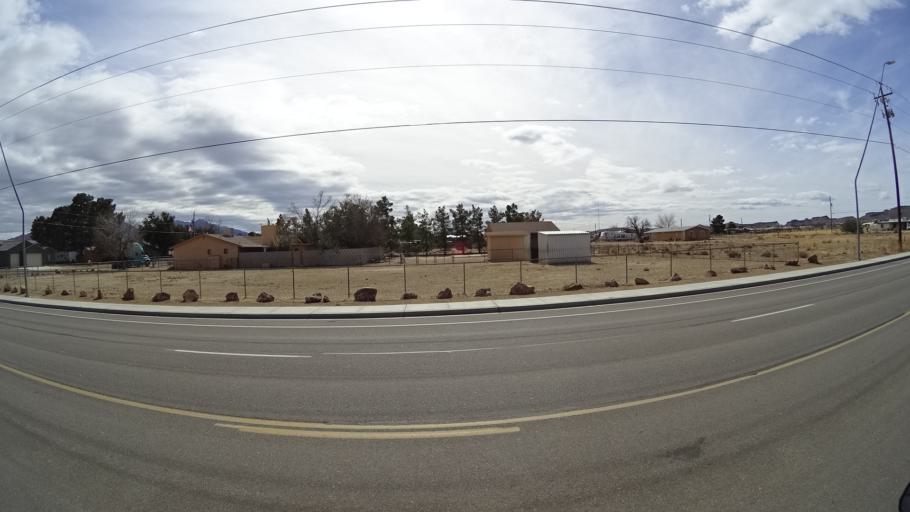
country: US
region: Arizona
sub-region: Mohave County
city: New Kingman-Butler
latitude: 35.2395
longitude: -114.0190
